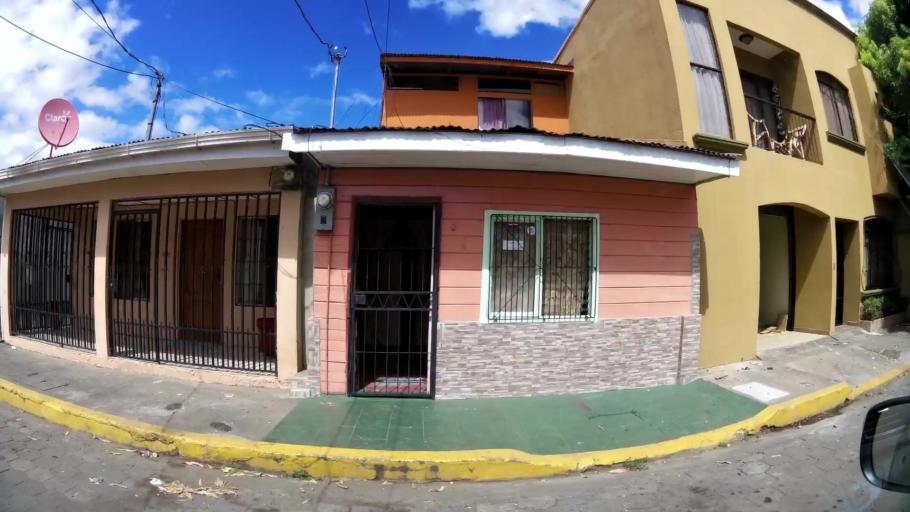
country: CR
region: Guanacaste
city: Santa Cruz
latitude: 10.2580
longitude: -85.5860
